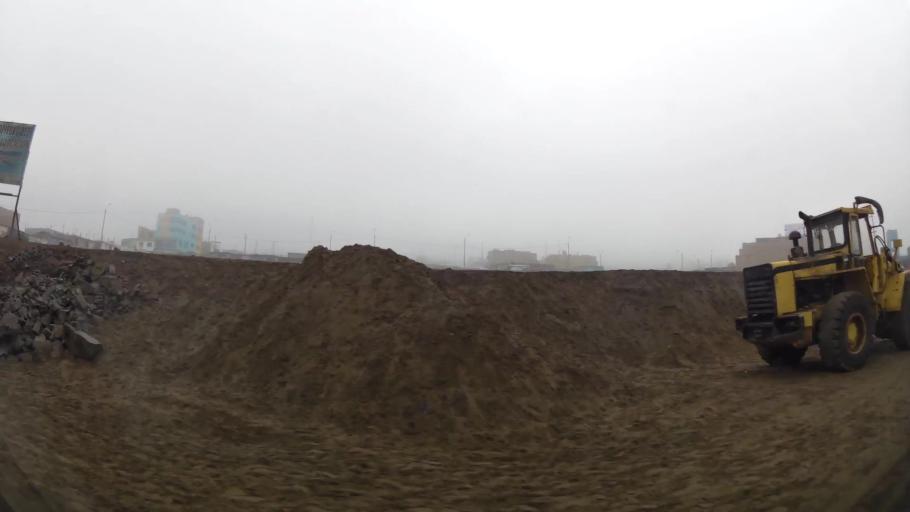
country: PE
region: Lima
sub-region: Lima
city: Santa Rosa
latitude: -11.8324
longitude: -77.1431
